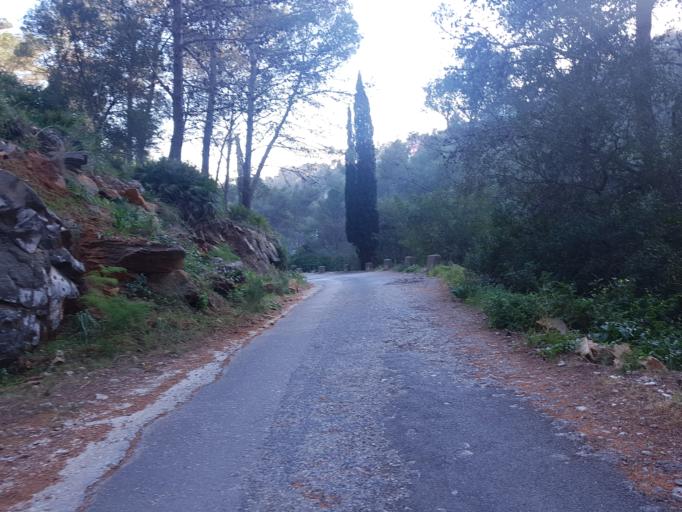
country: ES
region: Andalusia
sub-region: Provincia de Malaga
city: Marbella
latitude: 36.5328
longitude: -4.8840
